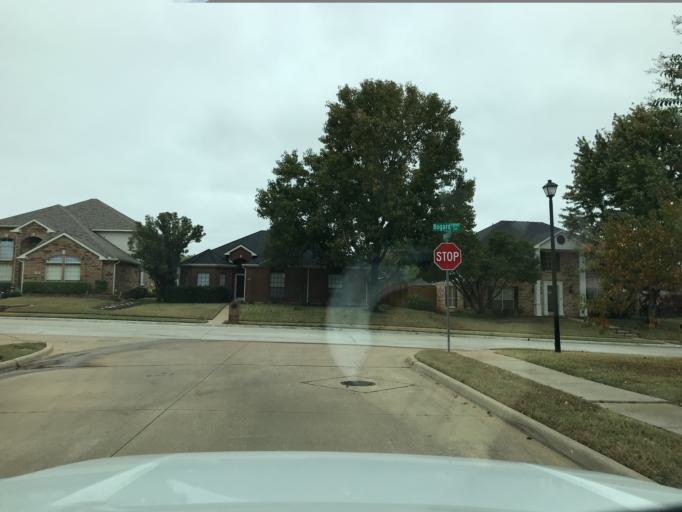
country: US
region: Texas
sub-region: Denton County
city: Highland Village
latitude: 33.0813
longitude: -97.0308
